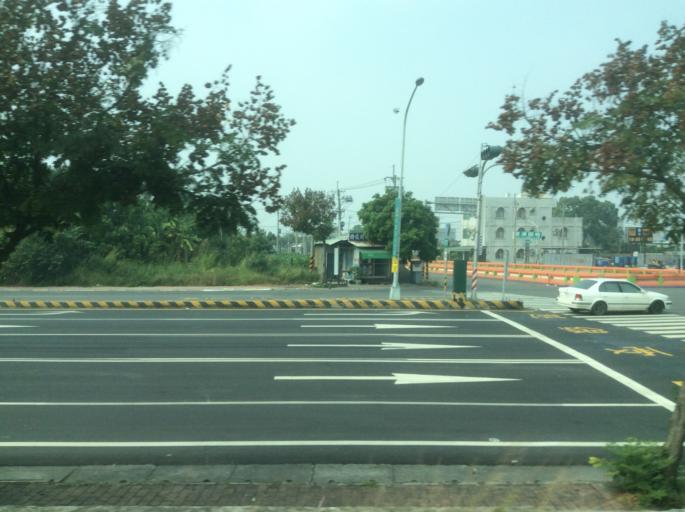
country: TW
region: Taiwan
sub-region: Chiayi
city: Taibao
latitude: 23.4265
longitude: 120.3938
